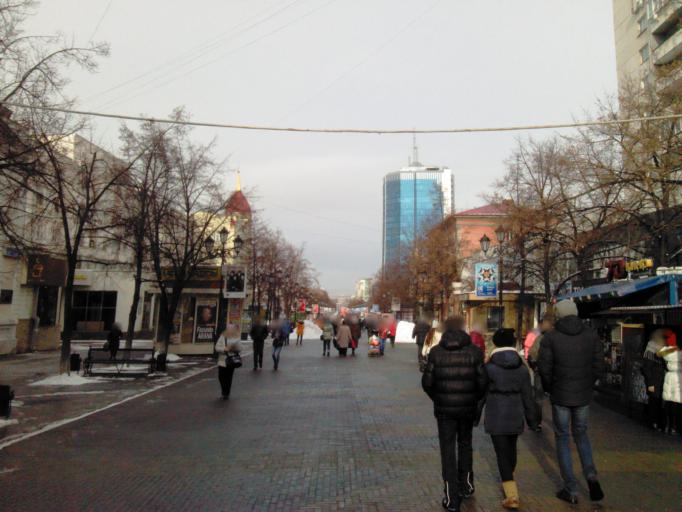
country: RU
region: Chelyabinsk
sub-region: Gorod Chelyabinsk
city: Chelyabinsk
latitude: 55.1611
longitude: 61.4008
